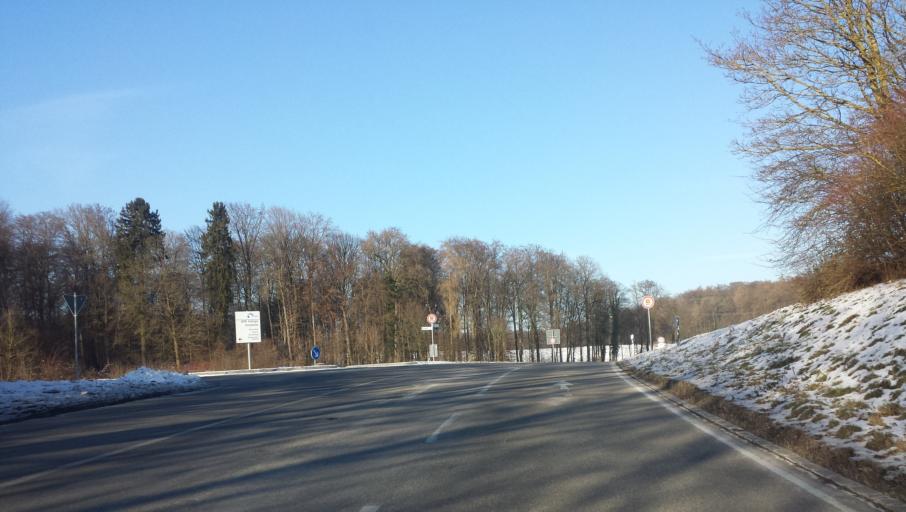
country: DE
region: Baden-Wuerttemberg
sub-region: Karlsruhe Region
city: Sinsheim
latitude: 49.2740
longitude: 8.8965
